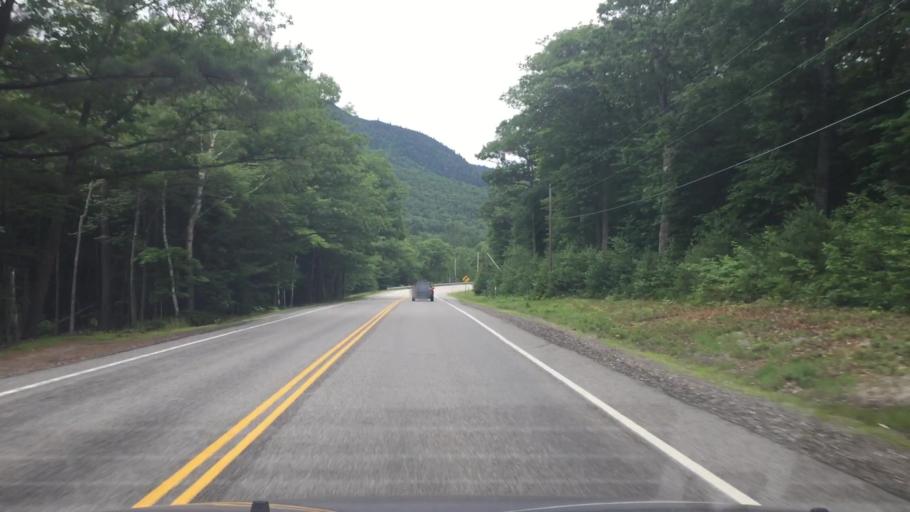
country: US
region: New Hampshire
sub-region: Carroll County
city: North Conway
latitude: 44.1233
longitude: -71.3563
